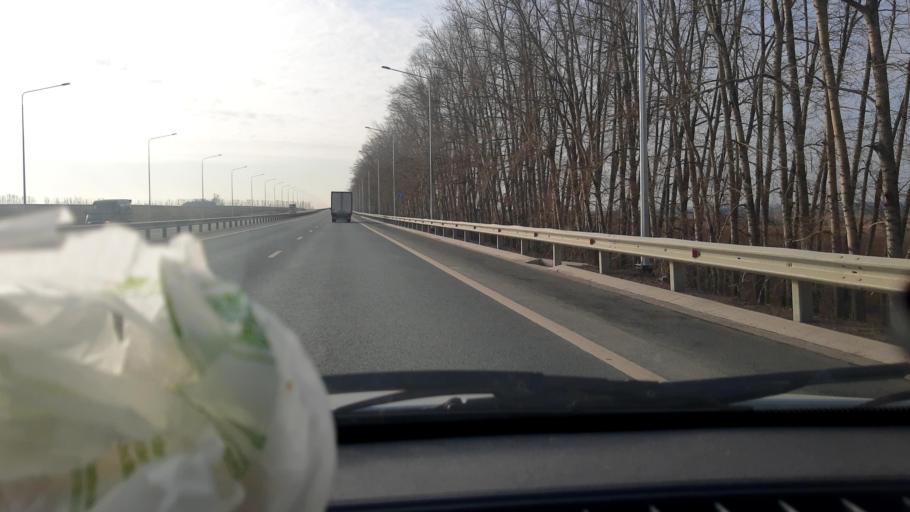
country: RU
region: Bashkortostan
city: Karmaskaly
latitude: 54.3384
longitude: 55.9013
